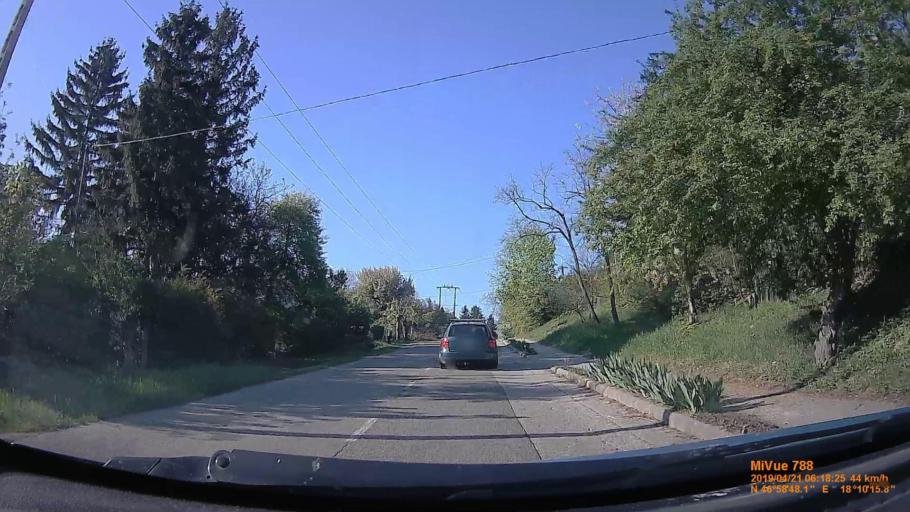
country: HU
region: Fejer
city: Lepseny
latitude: 46.9800
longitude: 18.1710
